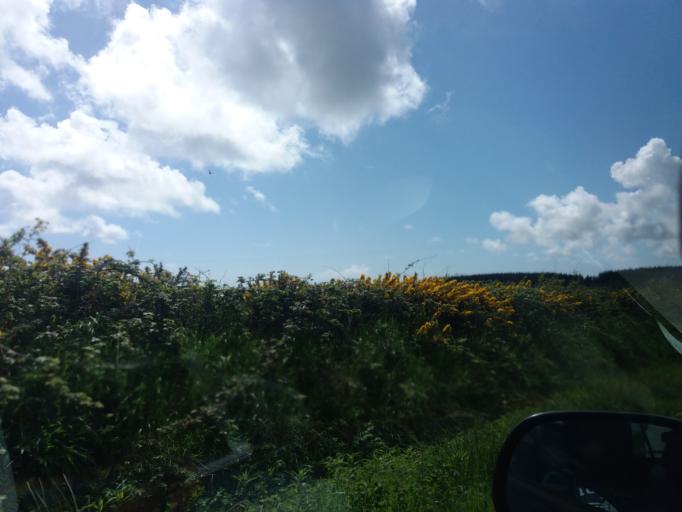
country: IE
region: Munster
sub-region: Waterford
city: Dunmore East
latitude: 52.2100
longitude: -6.8992
